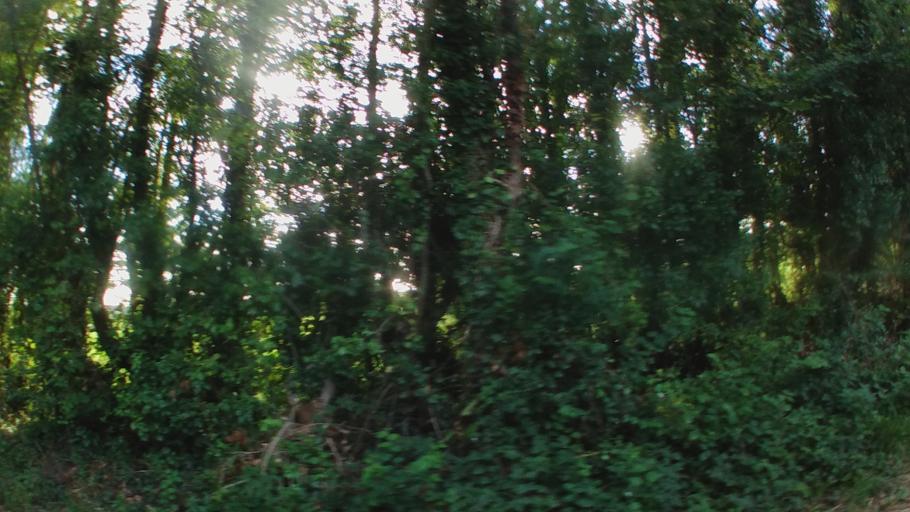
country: IE
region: Leinster
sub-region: Kilkenny
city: Kilkenny
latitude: 52.6767
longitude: -7.2255
